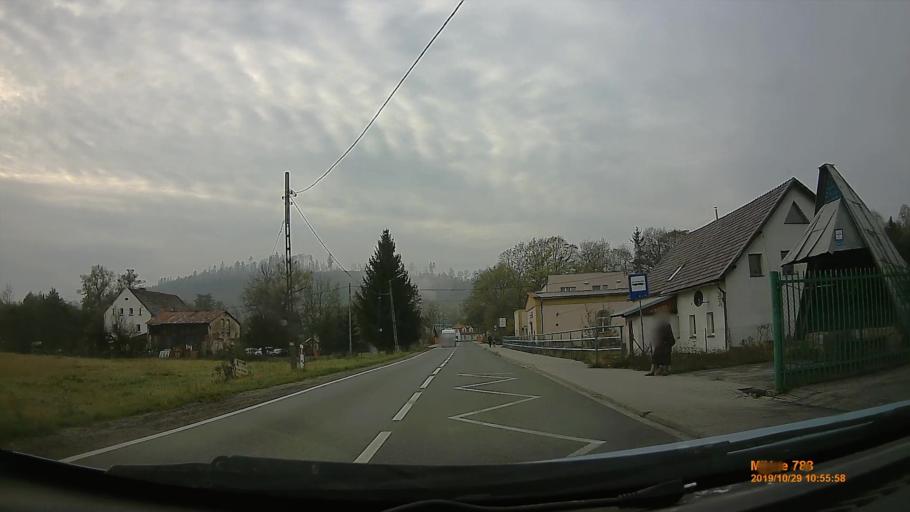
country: PL
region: Lower Silesian Voivodeship
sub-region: Powiat klodzki
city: Nowa Ruda
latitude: 50.5175
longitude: 16.4911
